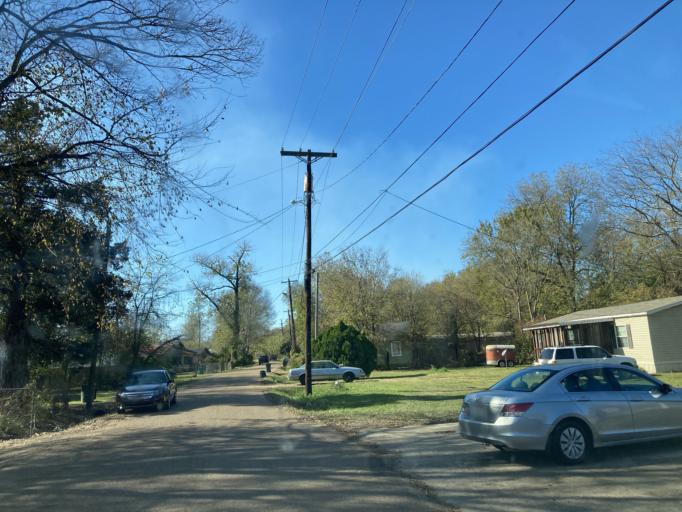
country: US
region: Mississippi
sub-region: Yazoo County
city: Yazoo City
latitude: 32.8532
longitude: -90.4149
